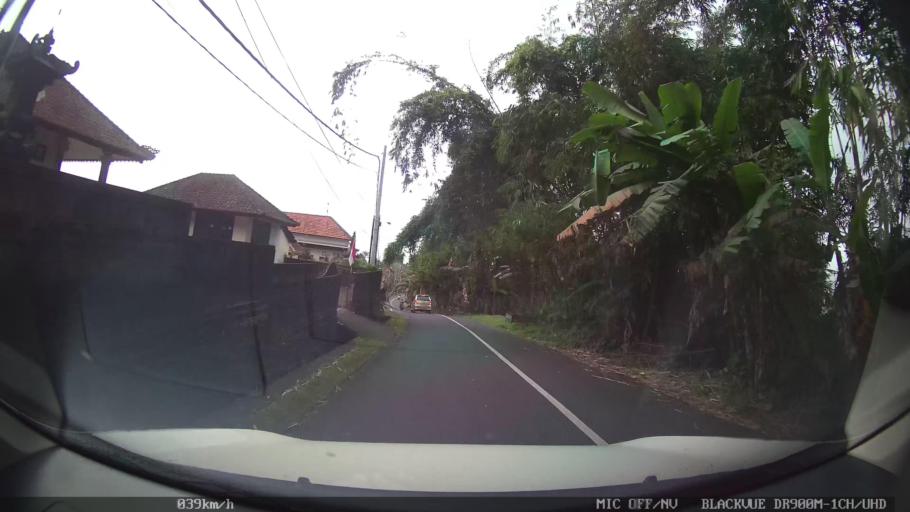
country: ID
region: Bali
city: Peneng
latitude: -8.3472
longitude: 115.1845
